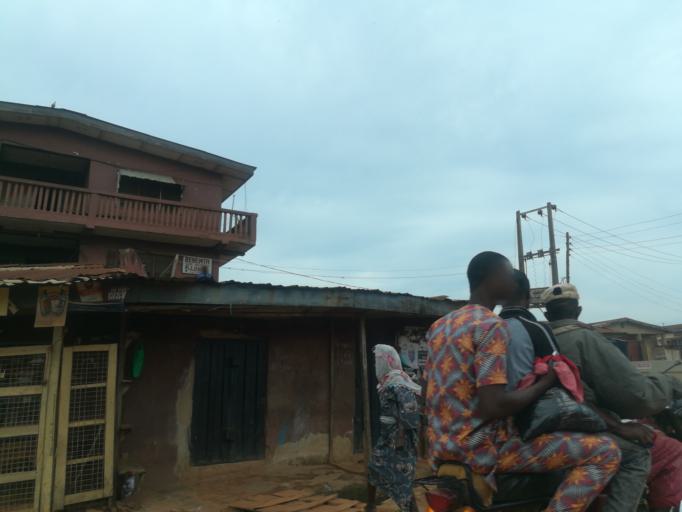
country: NG
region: Oyo
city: Ibadan
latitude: 7.3757
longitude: 3.9584
